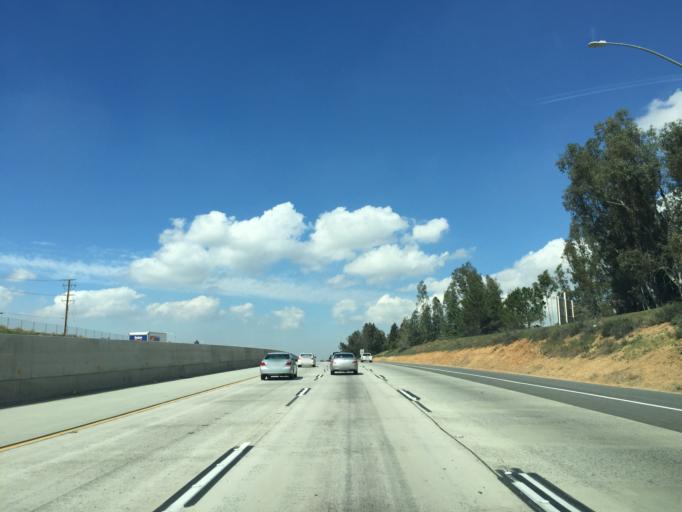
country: US
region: California
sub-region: Riverside County
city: Beaumont
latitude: 33.9481
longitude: -117.0060
